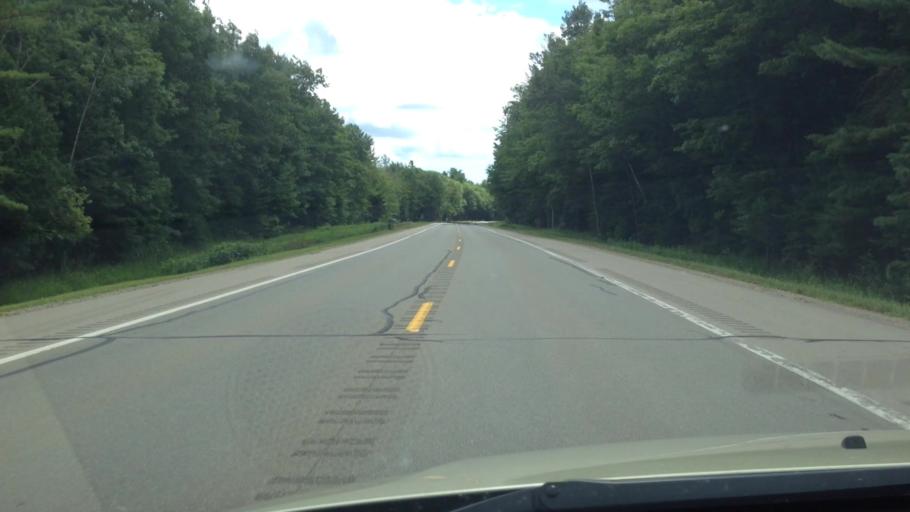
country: US
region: Michigan
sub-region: Menominee County
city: Menominee
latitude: 45.3030
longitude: -87.4396
